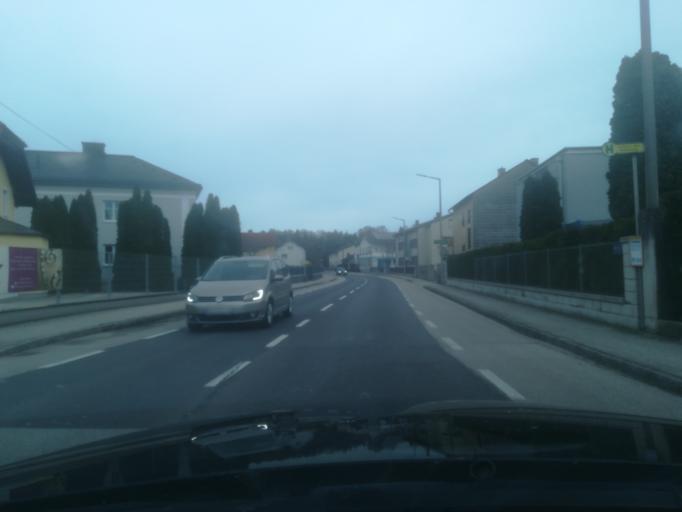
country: AT
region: Upper Austria
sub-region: Wels-Land
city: Thalheim bei Wels
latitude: 48.1536
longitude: 14.0373
